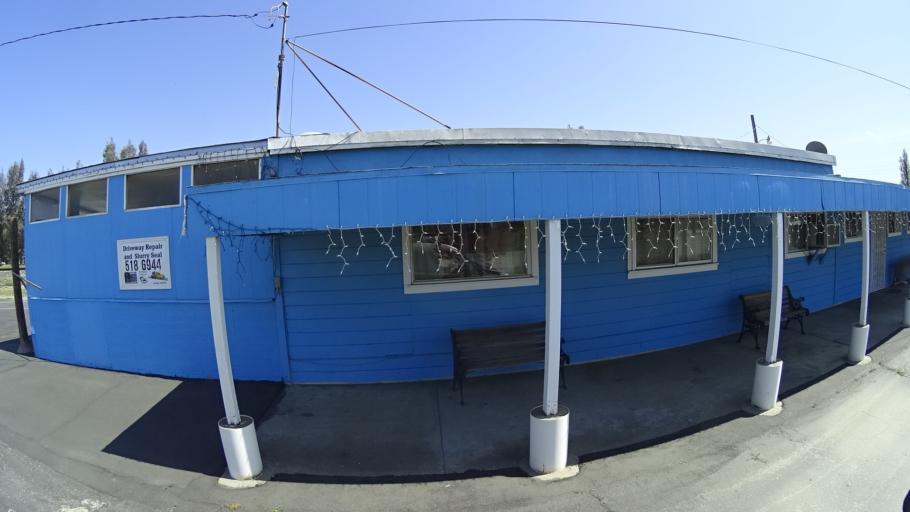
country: US
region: California
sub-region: Glenn County
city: Orland
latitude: 39.7269
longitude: -122.1969
